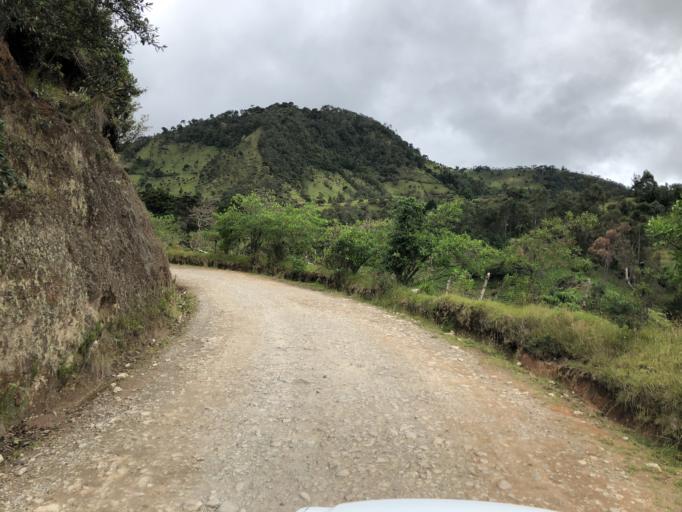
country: CO
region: Cauca
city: Totoro
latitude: 2.5092
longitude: -76.3653
